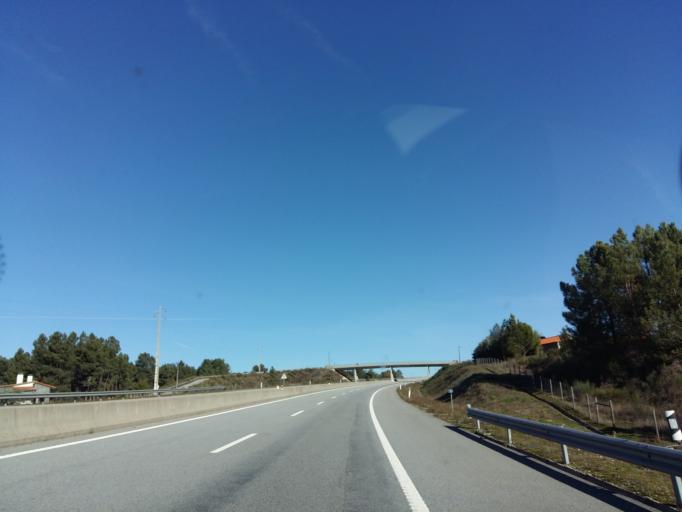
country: PT
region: Castelo Branco
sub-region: Covilha
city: Covilha
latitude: 40.2401
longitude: -7.4805
